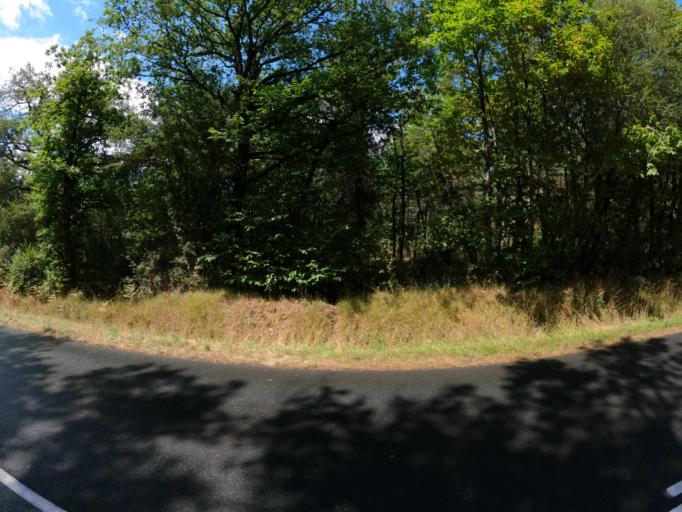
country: FR
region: Pays de la Loire
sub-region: Departement de Maine-et-Loire
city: Feneu
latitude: 47.6152
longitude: -0.5845
